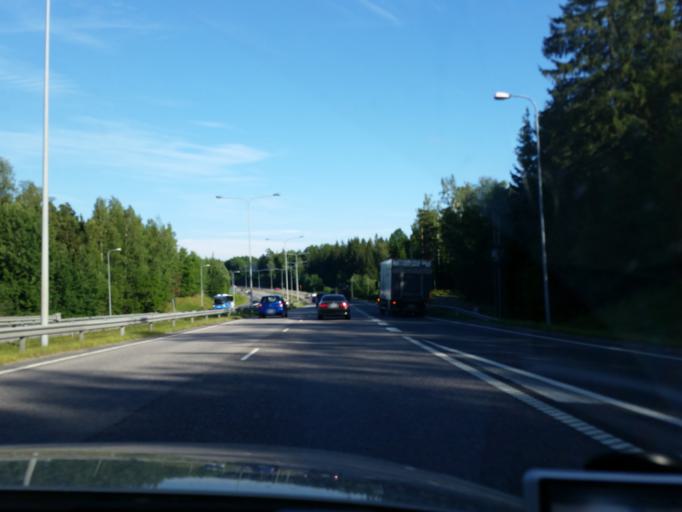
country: FI
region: Uusimaa
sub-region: Helsinki
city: Kauniainen
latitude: 60.2048
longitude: 24.6973
